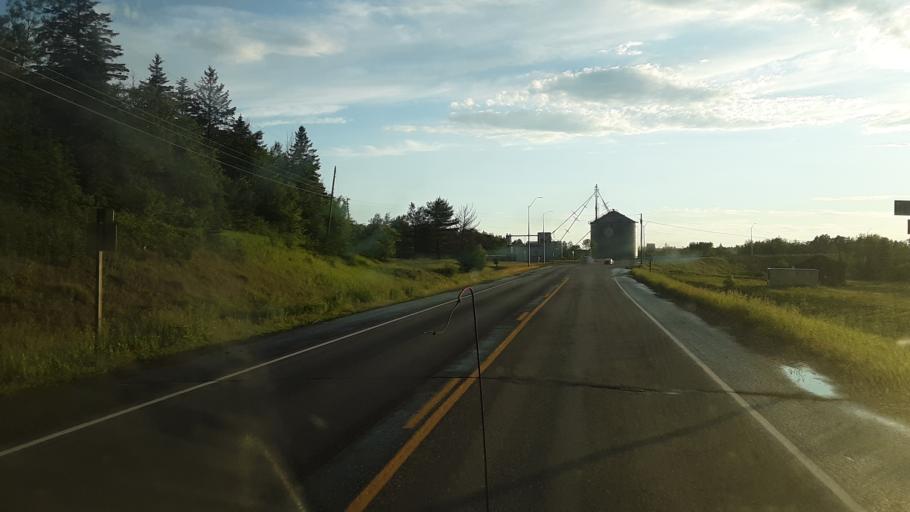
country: US
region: Maine
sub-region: Aroostook County
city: Presque Isle
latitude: 46.6935
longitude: -67.9943
